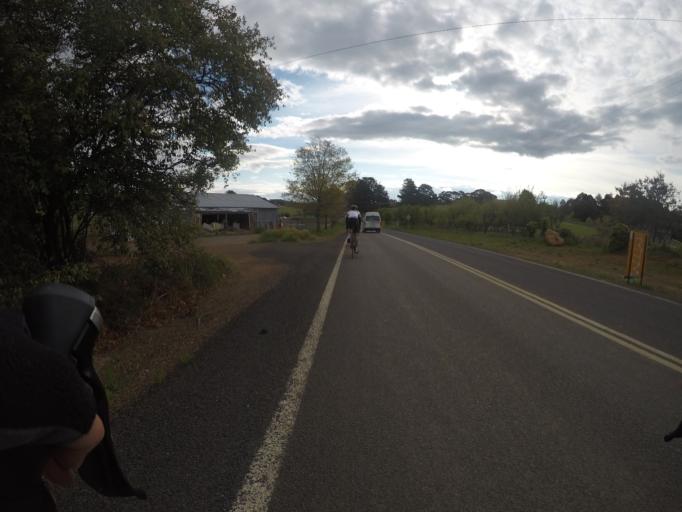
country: AU
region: New South Wales
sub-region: Orange Municipality
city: Orange
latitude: -33.2875
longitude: 149.0514
